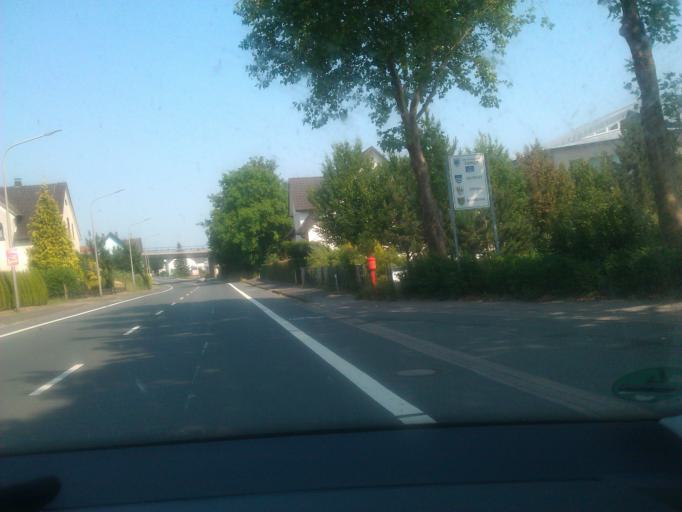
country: DE
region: North Rhine-Westphalia
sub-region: Regierungsbezirk Detmold
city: Lemgo
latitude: 52.0289
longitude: 8.8706
